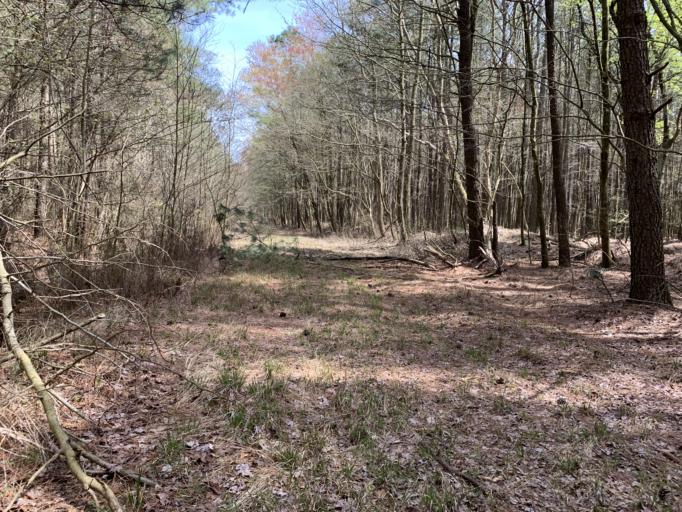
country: US
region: Delaware
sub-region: Sussex County
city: Millsboro
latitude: 38.5389
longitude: -75.3884
